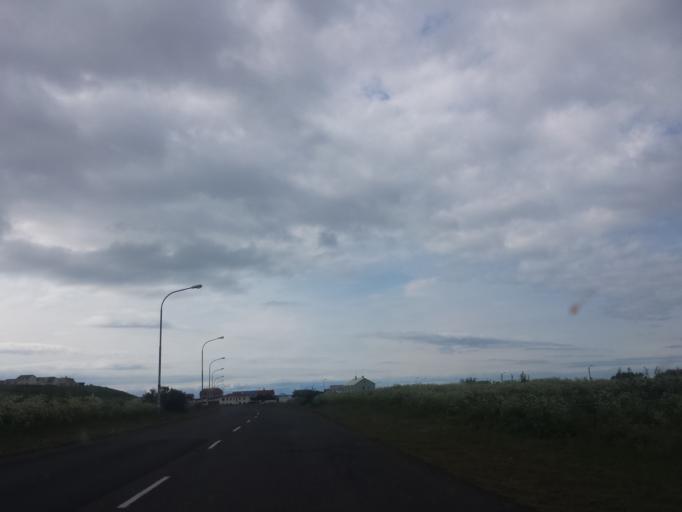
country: IS
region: Northwest
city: Saudarkrokur
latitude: 65.6580
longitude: -20.2934
